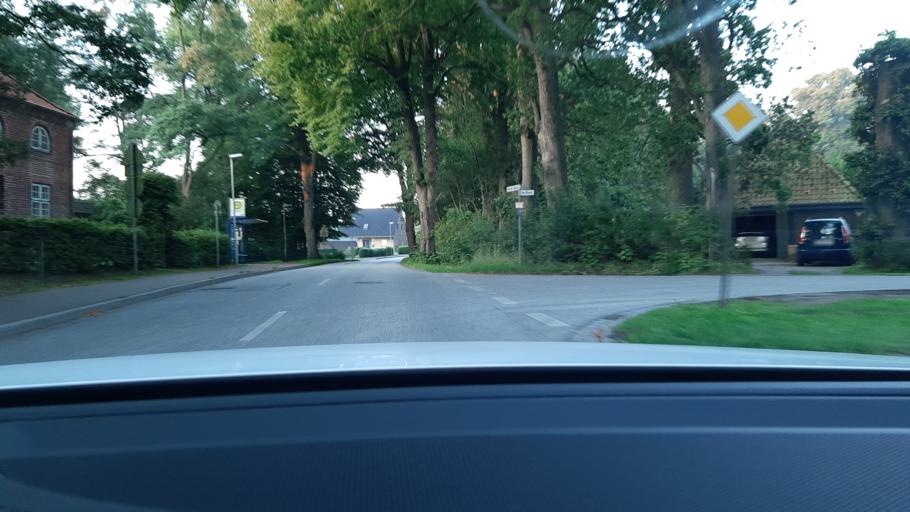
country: DE
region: Schleswig-Holstein
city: Hamberge
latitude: 53.8326
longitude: 10.6097
